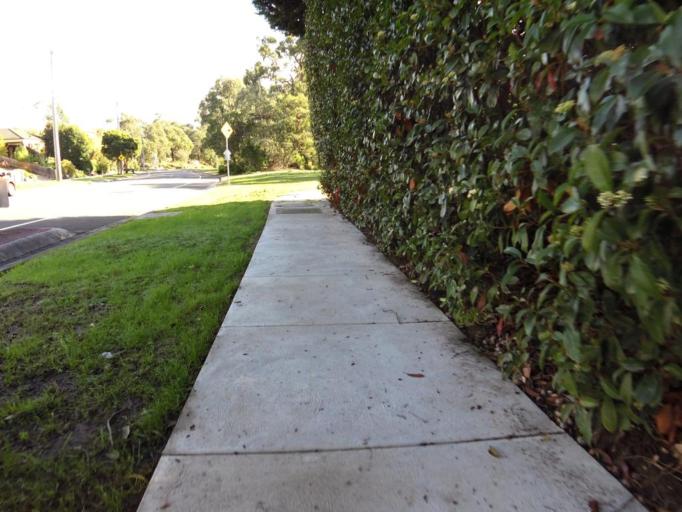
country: AU
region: Victoria
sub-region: Maroondah
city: Croydon Hills
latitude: -37.7732
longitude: 145.2730
